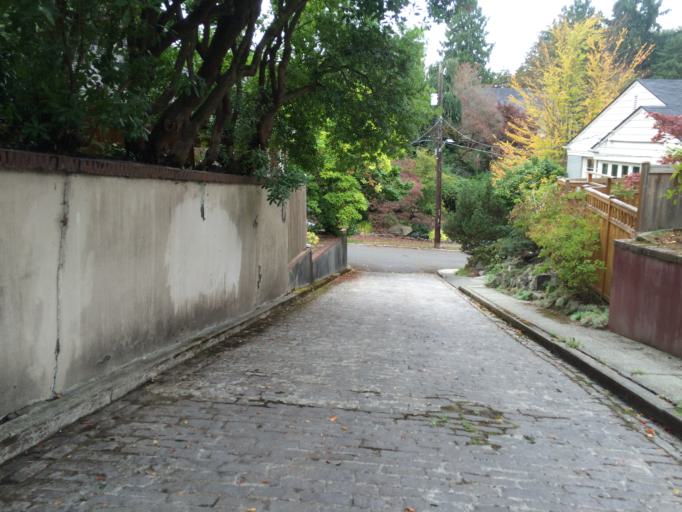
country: US
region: Washington
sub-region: King County
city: Seattle
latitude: 47.6348
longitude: -122.3038
